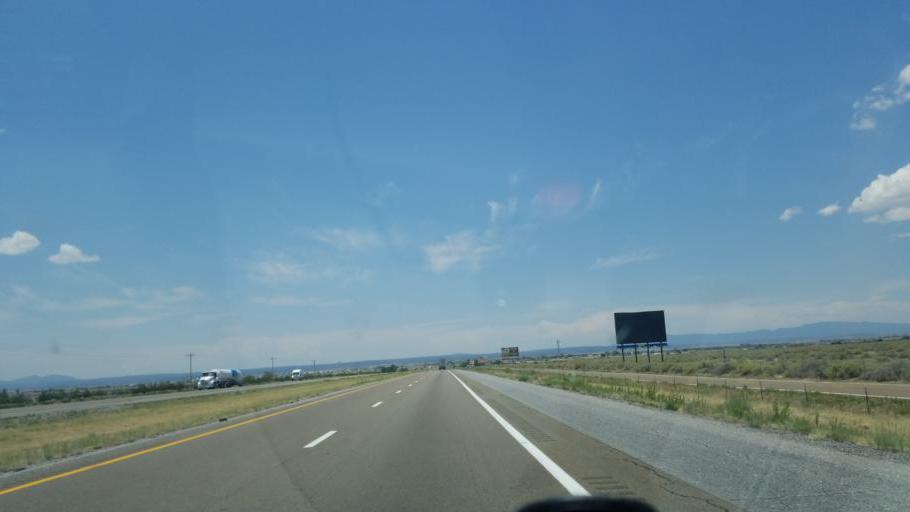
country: US
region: New Mexico
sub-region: Torrance County
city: Moriarty
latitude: 35.0049
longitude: -105.9844
